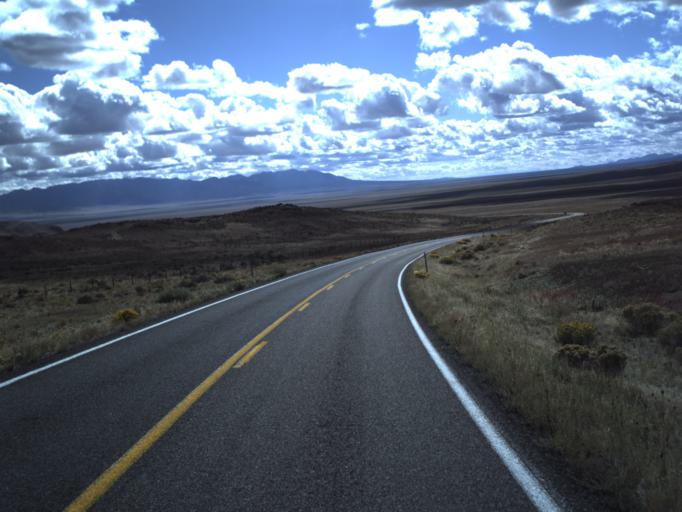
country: US
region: Utah
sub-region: Beaver County
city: Milford
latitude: 38.6108
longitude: -113.8360
